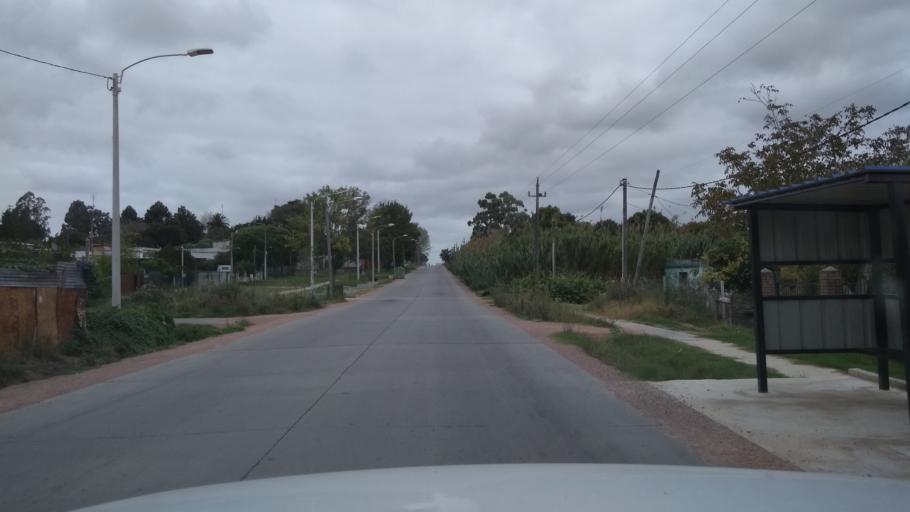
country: UY
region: Canelones
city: Toledo
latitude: -34.7847
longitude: -56.1400
